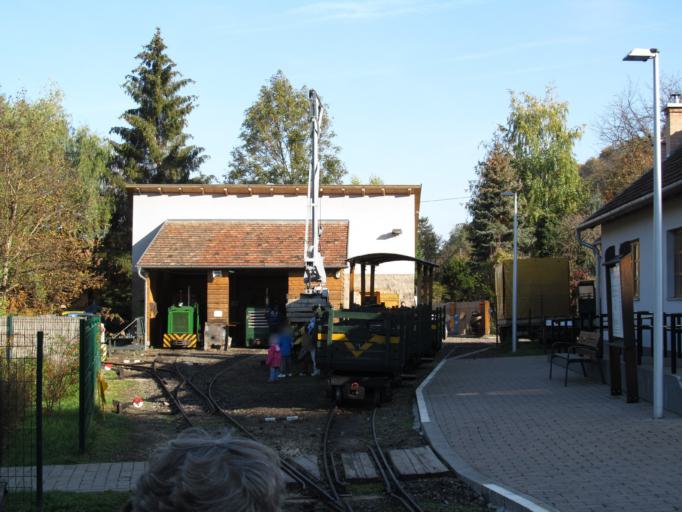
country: SK
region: Nitriansky
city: Sahy
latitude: 48.0134
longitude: 18.8941
